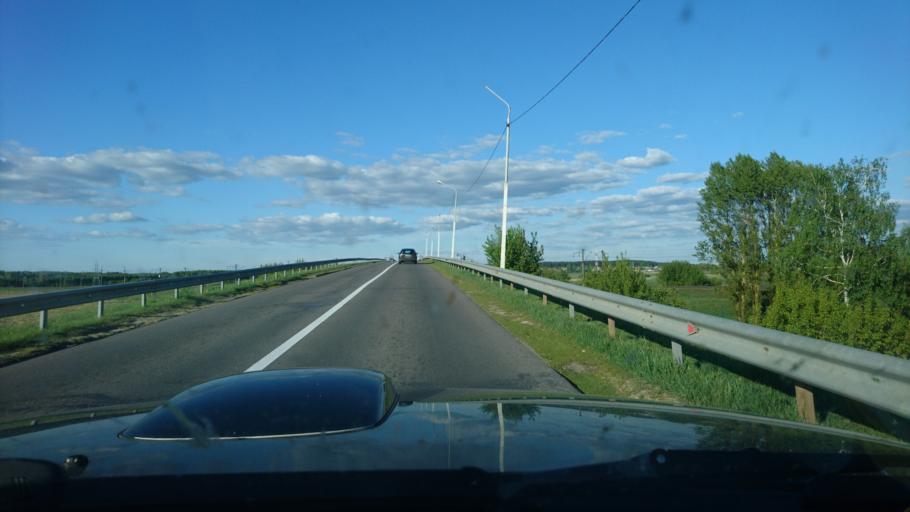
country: BY
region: Brest
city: Ivatsevichy
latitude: 52.7181
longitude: 25.3558
